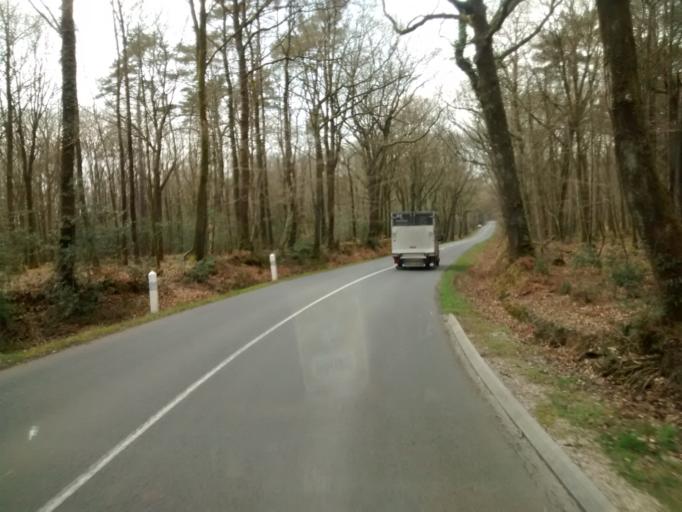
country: FR
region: Brittany
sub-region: Departement d'Ille-et-Vilaine
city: Paimpont
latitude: 48.0140
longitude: -2.1496
